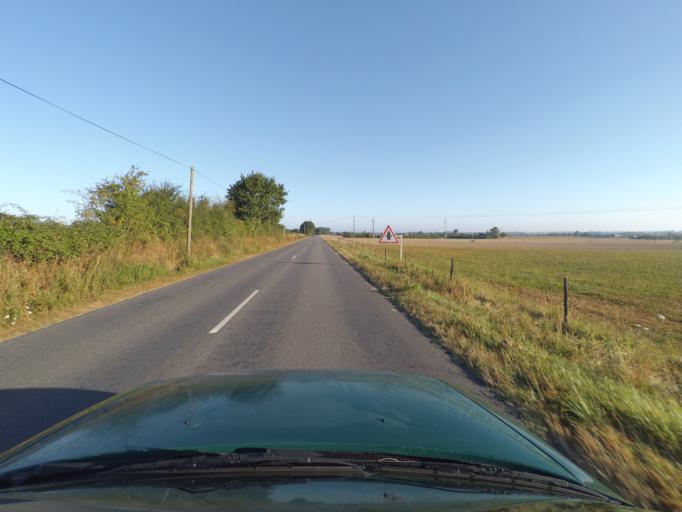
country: FR
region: Pays de la Loire
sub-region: Departement de la Loire-Atlantique
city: Vieillevigne
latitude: 46.9899
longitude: -1.4478
